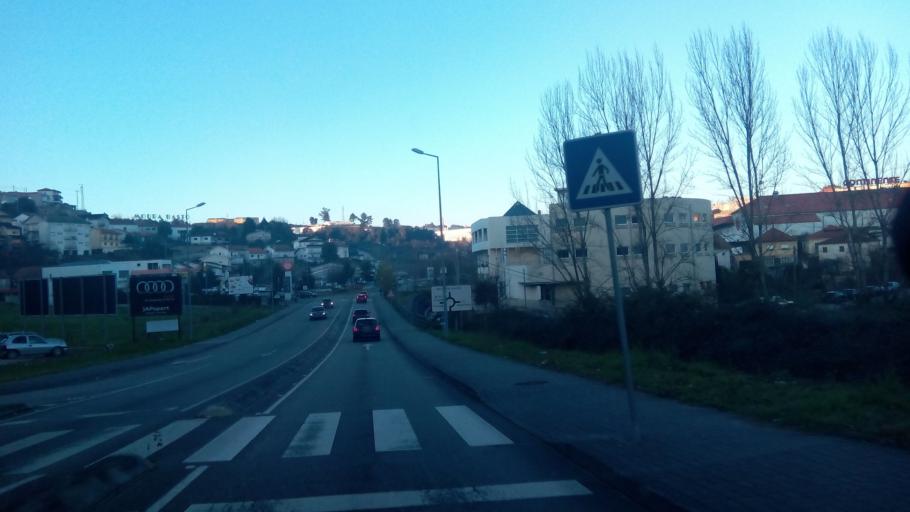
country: PT
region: Porto
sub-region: Amarante
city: Amarante
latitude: 41.2713
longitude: -8.0890
